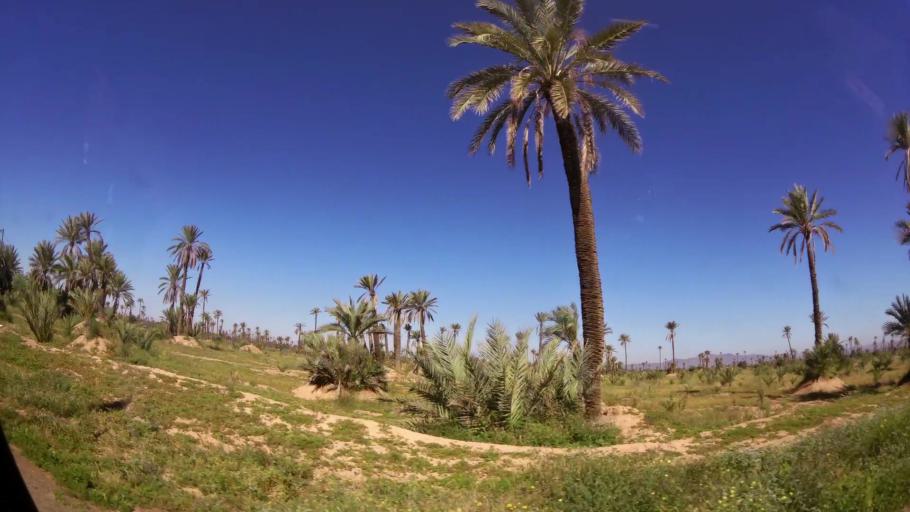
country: MA
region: Marrakech-Tensift-Al Haouz
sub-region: Marrakech
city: Marrakesh
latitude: 31.6612
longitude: -7.9468
